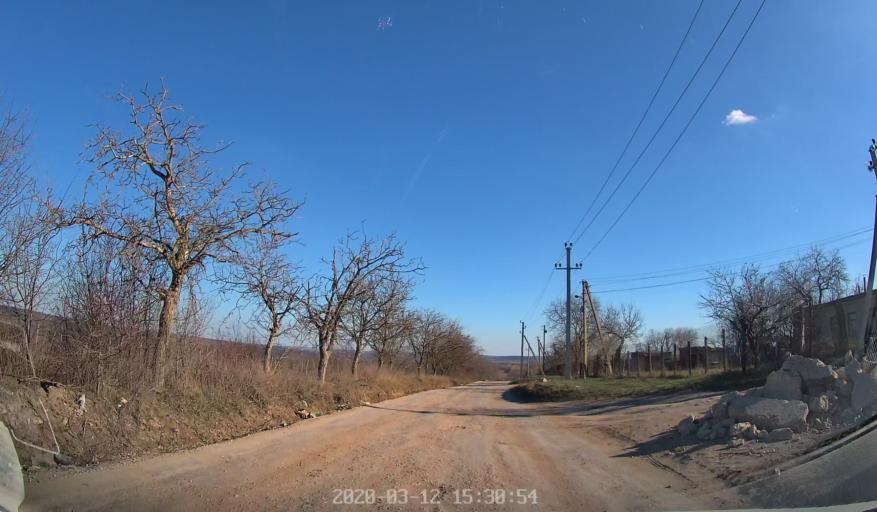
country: MD
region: Chisinau
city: Ciorescu
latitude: 47.1592
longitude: 28.9407
